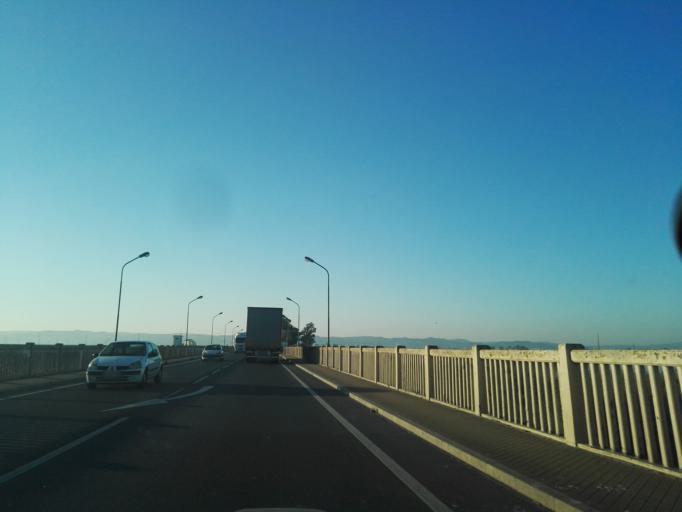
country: PT
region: Santarem
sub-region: Benavente
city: Samora Correia
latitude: 38.9248
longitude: -8.8914
